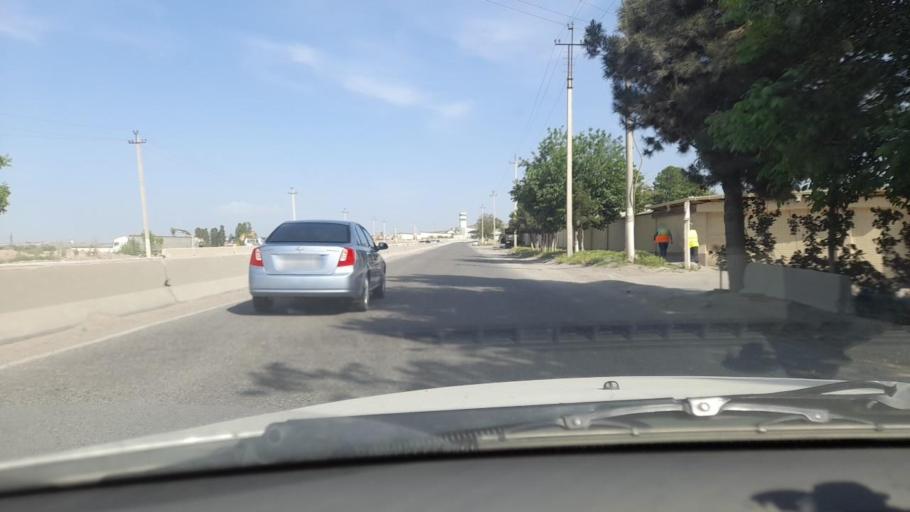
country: UZ
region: Samarqand
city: Samarqand
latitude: 39.7010
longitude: 67.0135
